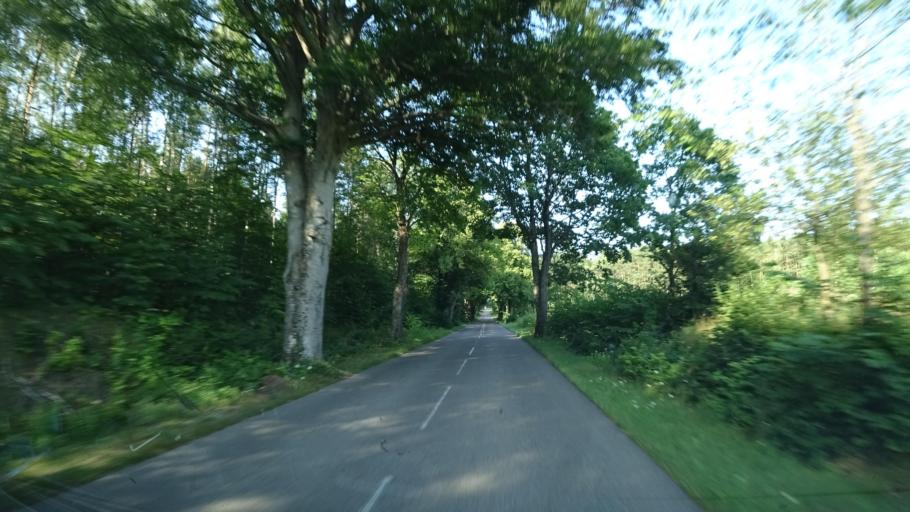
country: PL
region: Pomeranian Voivodeship
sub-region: Powiat czluchowski
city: Rzeczenica
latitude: 53.7657
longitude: 17.1419
